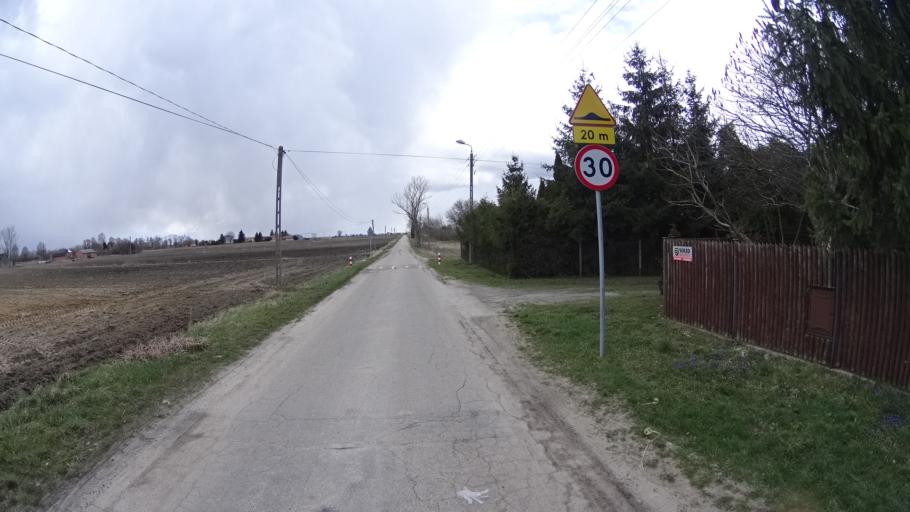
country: PL
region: Masovian Voivodeship
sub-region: Powiat warszawski zachodni
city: Jozefow
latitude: 52.2213
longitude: 20.6846
